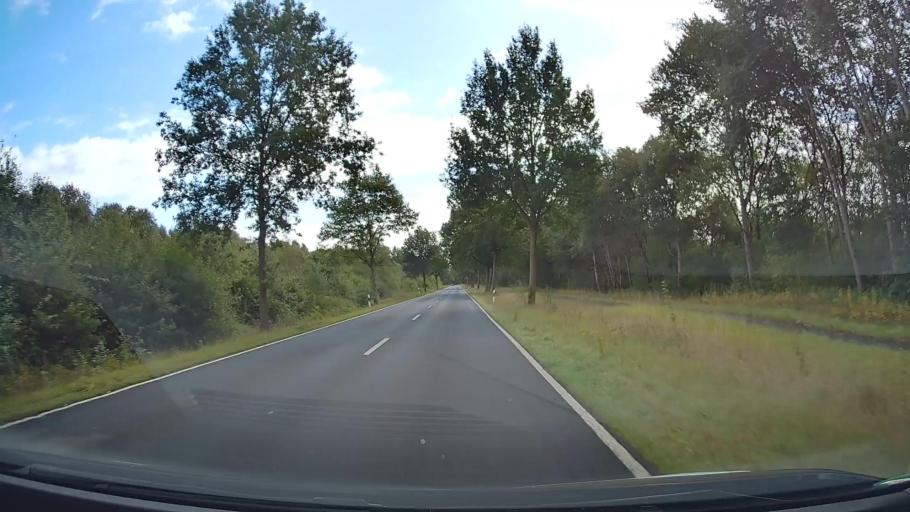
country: DE
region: Lower Saxony
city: Rhade
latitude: 53.3425
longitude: 9.0879
